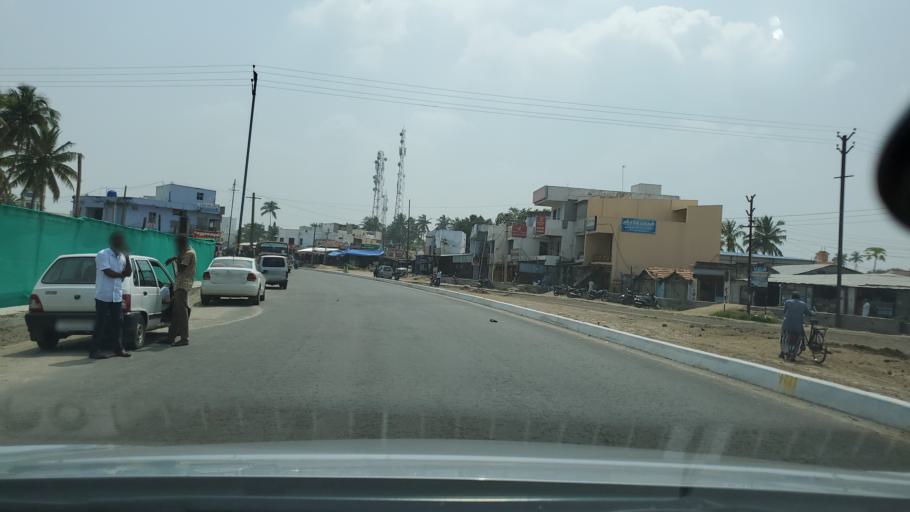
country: IN
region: Tamil Nadu
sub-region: Tiruppur
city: Kangayam
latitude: 10.9441
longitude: 77.4362
